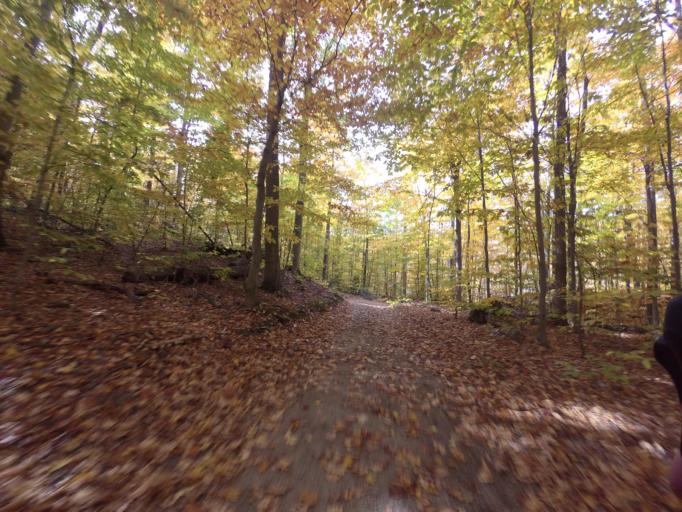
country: CA
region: Quebec
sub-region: Outaouais
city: Gatineau
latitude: 45.4756
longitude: -75.8021
